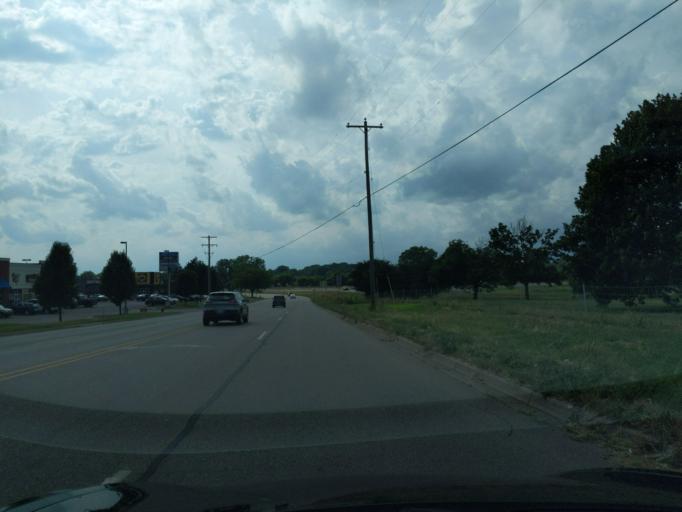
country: US
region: Michigan
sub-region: Jackson County
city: Jackson
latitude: 42.2701
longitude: -84.4265
